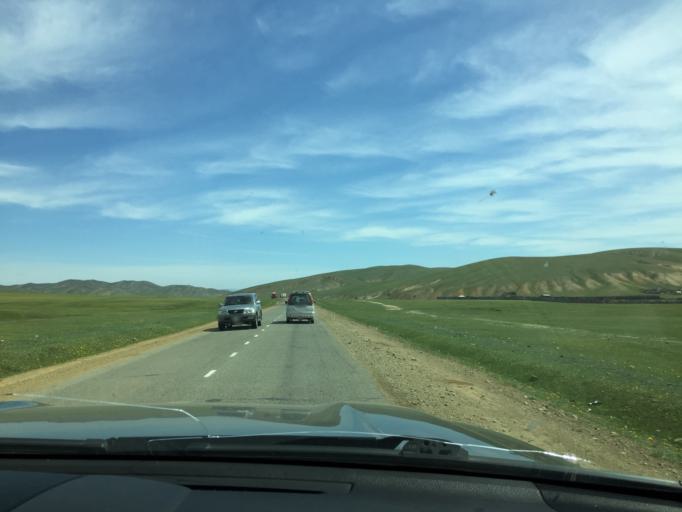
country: MN
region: Central Aimak
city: Bornuur
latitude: 48.6664
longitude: 106.1309
